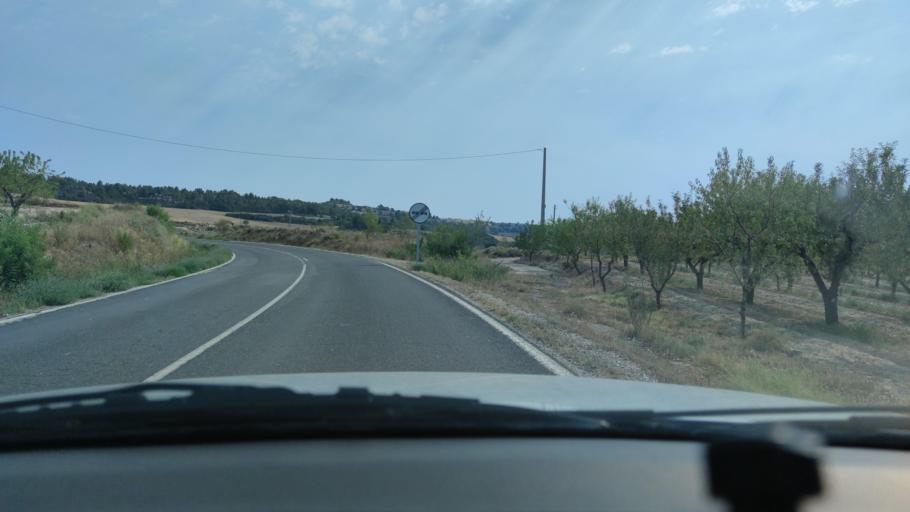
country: ES
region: Catalonia
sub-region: Provincia de Lleida
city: Arbeca
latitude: 41.5022
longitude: 0.9699
